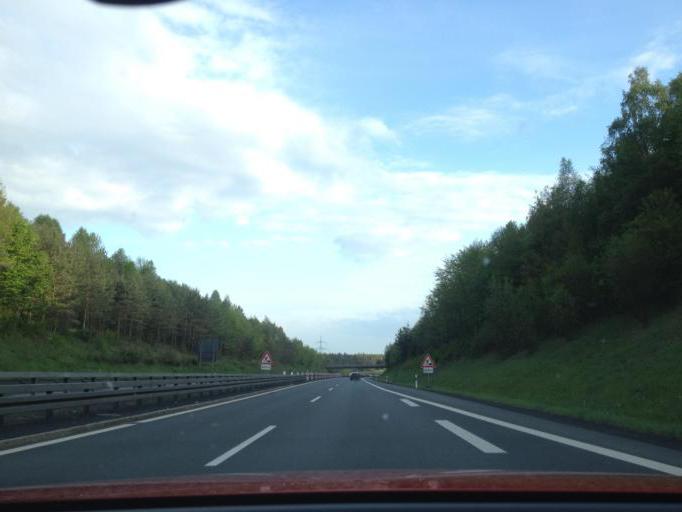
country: DE
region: Bavaria
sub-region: Upper Palatinate
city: Wiesau
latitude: 49.9099
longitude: 12.2200
